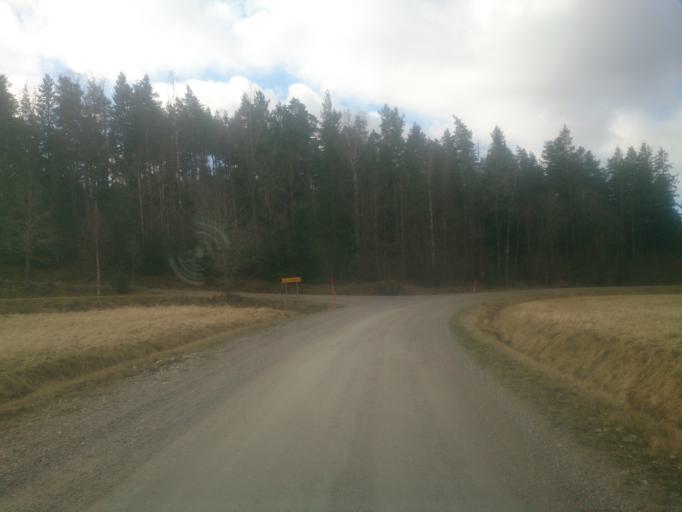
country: SE
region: OEstergoetland
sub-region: Atvidabergs Kommun
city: Atvidaberg
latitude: 58.2083
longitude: 16.1673
